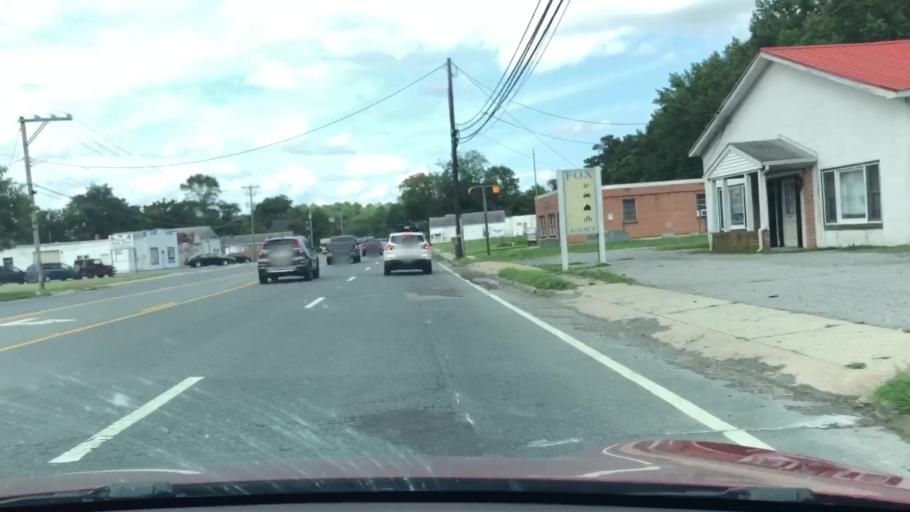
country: US
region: Virginia
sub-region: Accomack County
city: Wattsville
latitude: 37.8904
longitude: -75.5504
